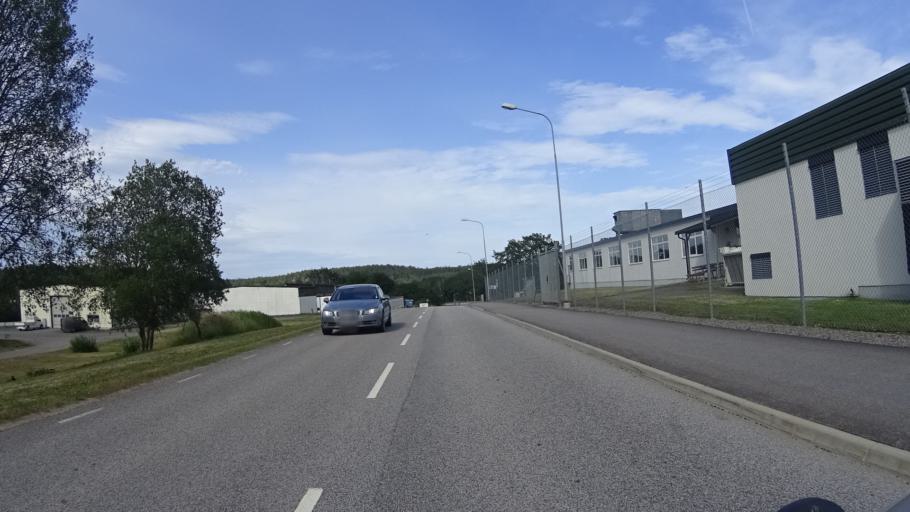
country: SE
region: Kalmar
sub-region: Vasterviks Kommun
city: Gamleby
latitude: 57.8890
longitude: 16.4111
